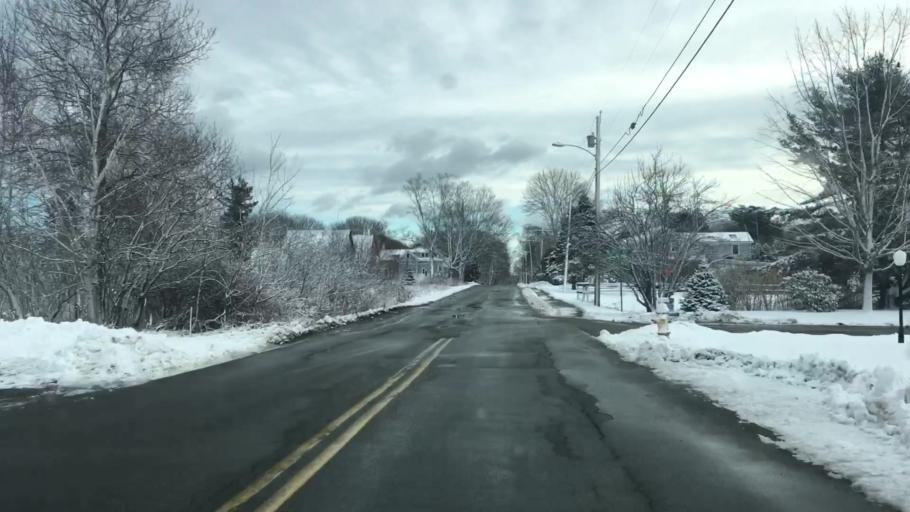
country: US
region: Maine
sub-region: Knox County
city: Rockland
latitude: 44.1097
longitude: -69.1235
